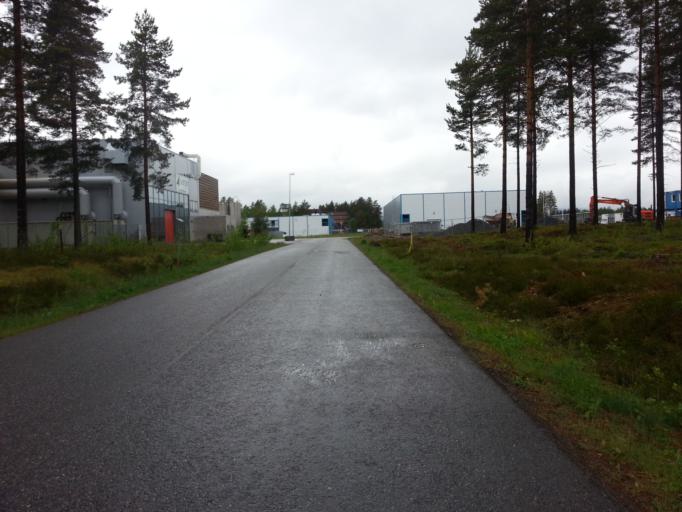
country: NO
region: Buskerud
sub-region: Ringerike
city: Honefoss
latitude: 60.1431
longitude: 10.2562
